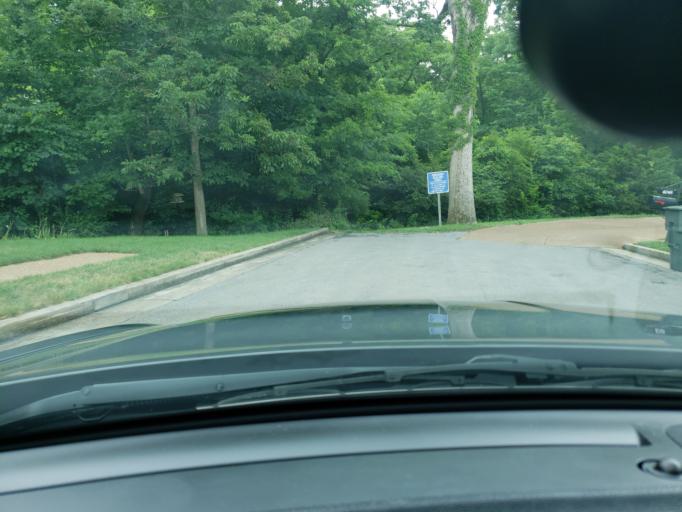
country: US
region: Tennessee
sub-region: Williamson County
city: Nolensville
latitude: 36.0187
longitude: -86.6965
